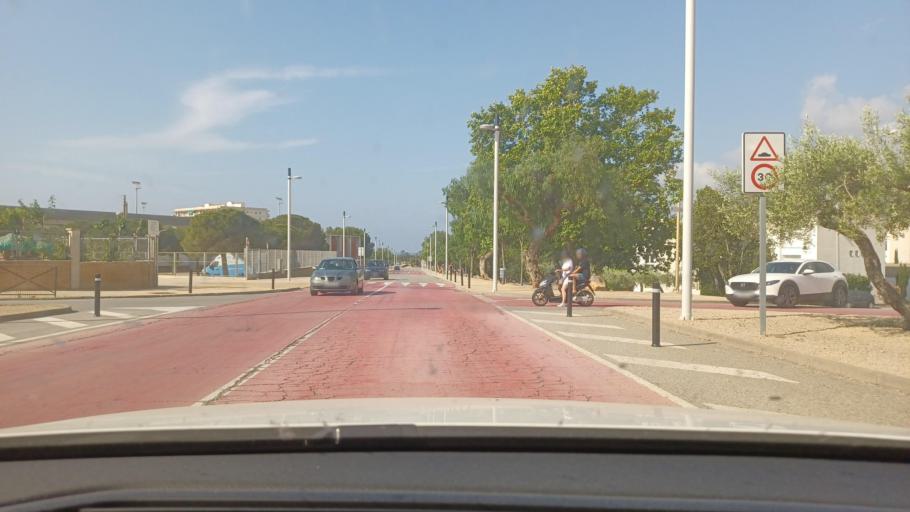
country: ES
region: Catalonia
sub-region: Provincia de Tarragona
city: Colldejou
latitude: 40.9930
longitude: 0.9189
